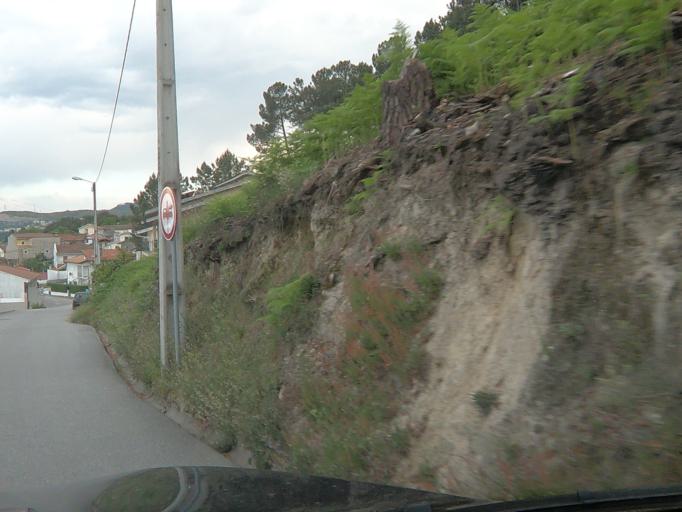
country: PT
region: Vila Real
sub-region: Vila Real
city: Vila Real
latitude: 41.3072
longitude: -7.7796
